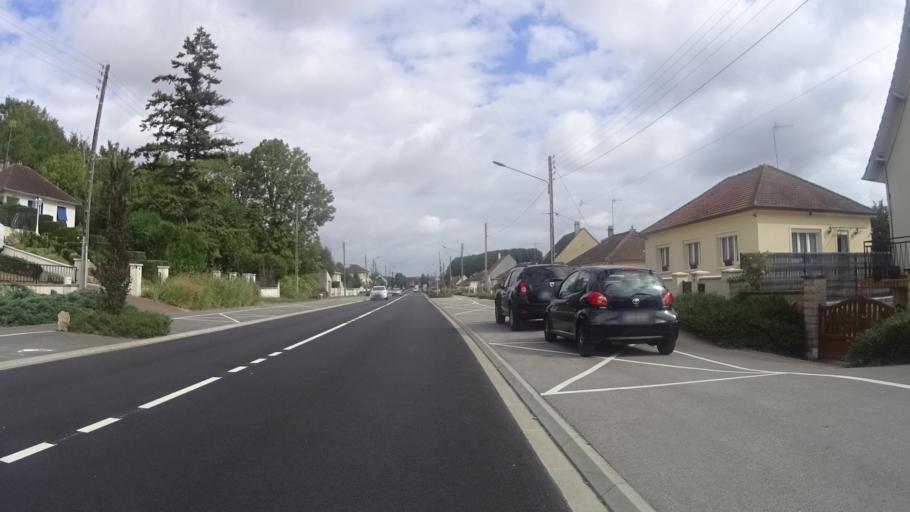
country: FR
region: Picardie
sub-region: Departement de l'Oise
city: Choisy-au-Bac
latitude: 49.4453
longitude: 2.8639
